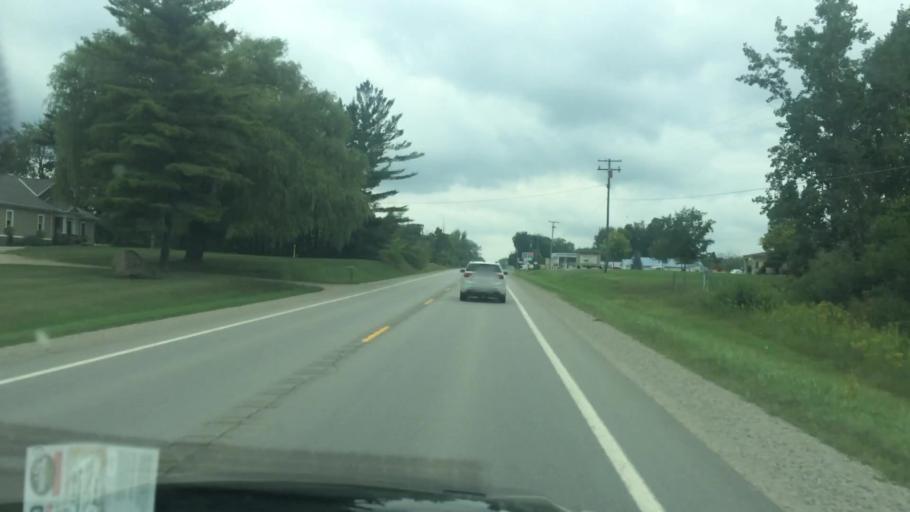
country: US
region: Michigan
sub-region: Tuscola County
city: Cass City
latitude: 43.5969
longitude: -83.0966
